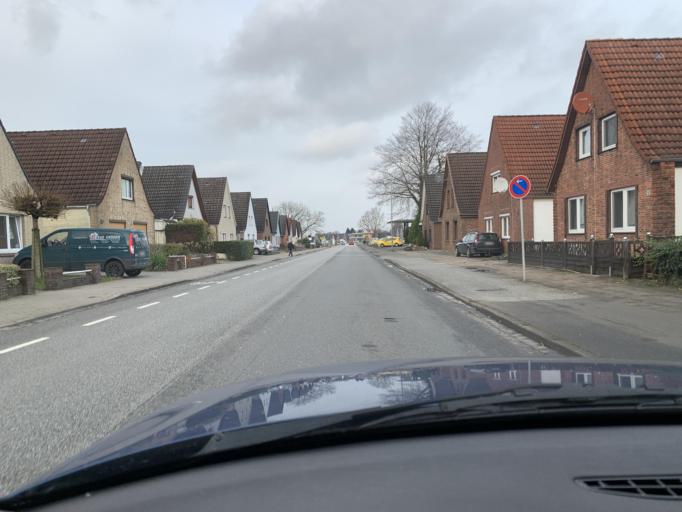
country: DE
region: Schleswig-Holstein
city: Wesseln
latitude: 54.2037
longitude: 9.0888
